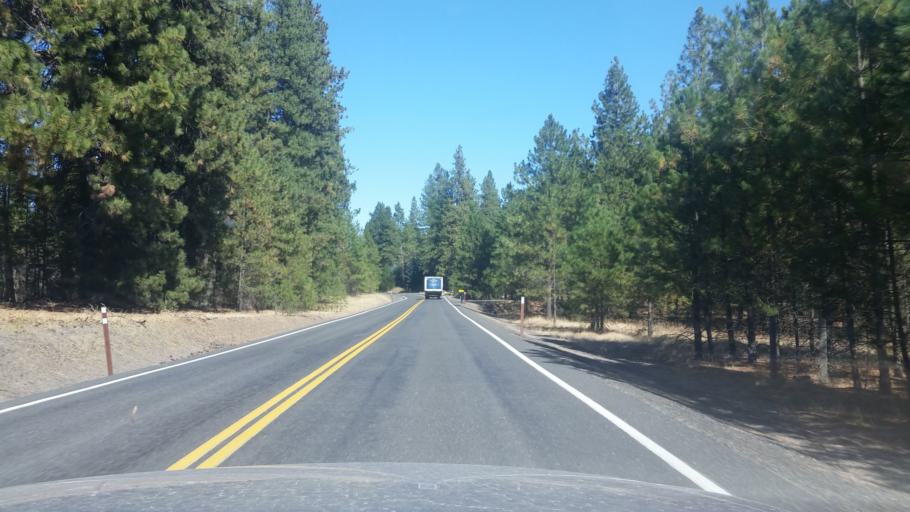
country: US
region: Washington
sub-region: Spokane County
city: Spokane
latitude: 47.5745
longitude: -117.4678
